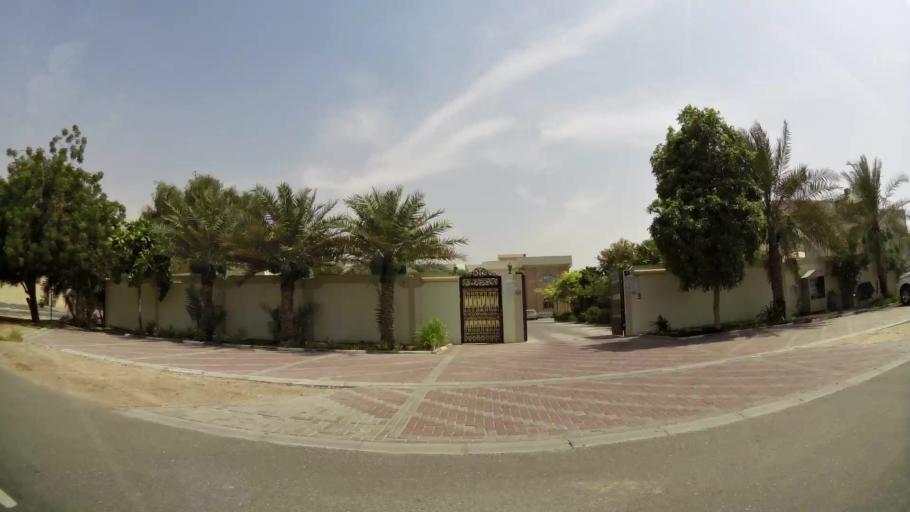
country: AE
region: Ash Shariqah
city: Sharjah
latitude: 25.2409
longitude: 55.4321
